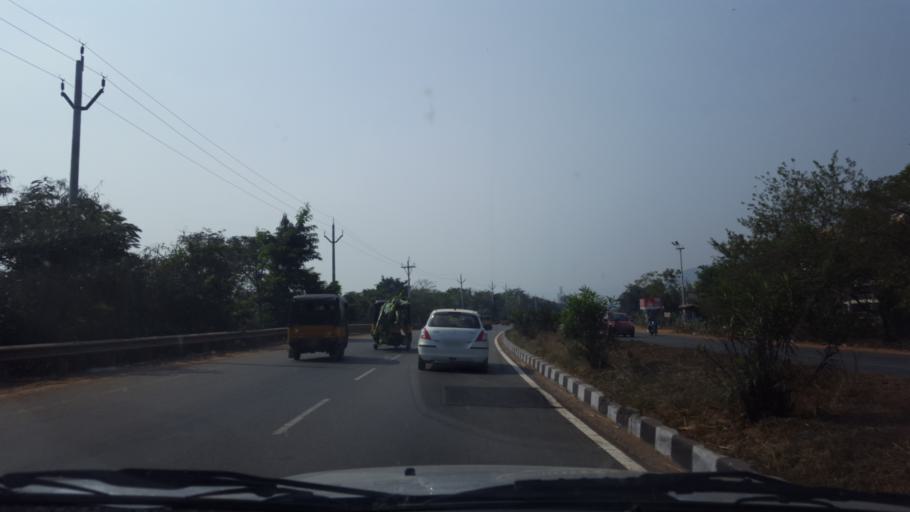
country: IN
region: Andhra Pradesh
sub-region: Vishakhapatnam
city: Bhimunipatnam
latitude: 17.8859
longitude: 83.3780
